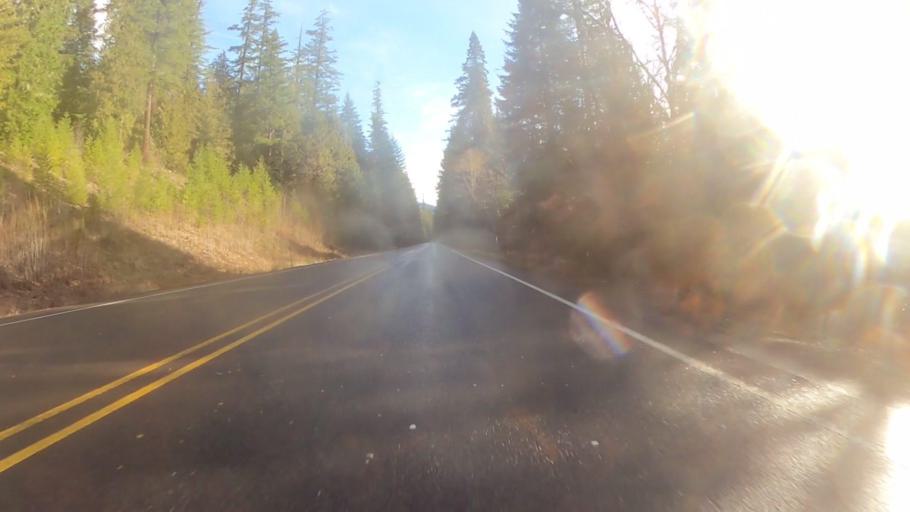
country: US
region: Oregon
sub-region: Lane County
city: Oakridge
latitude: 43.6940
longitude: -122.2663
